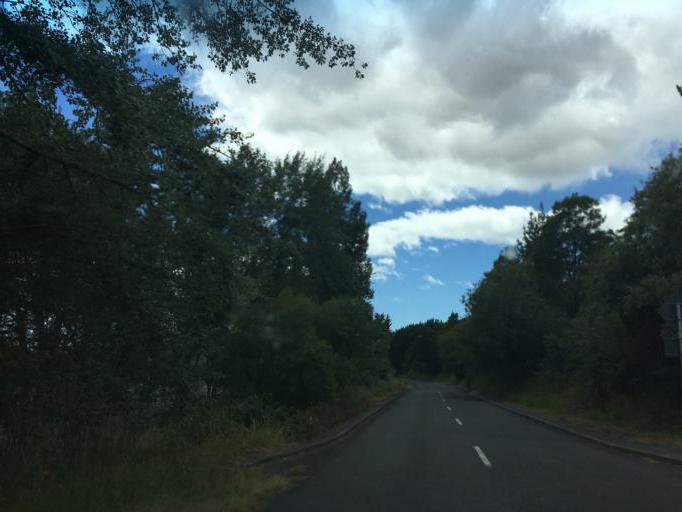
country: NZ
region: Hawke's Bay
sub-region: Hastings District
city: Hastings
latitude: -39.7349
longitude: 176.9004
